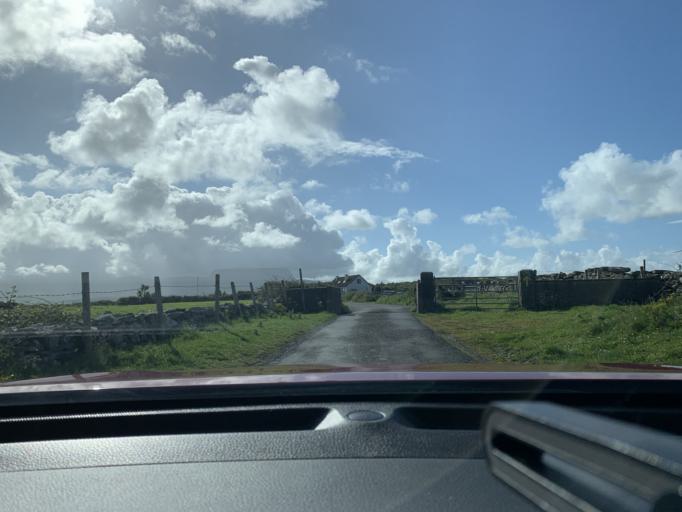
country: IE
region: Connaught
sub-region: Sligo
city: Strandhill
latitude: 54.3973
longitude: -8.5663
